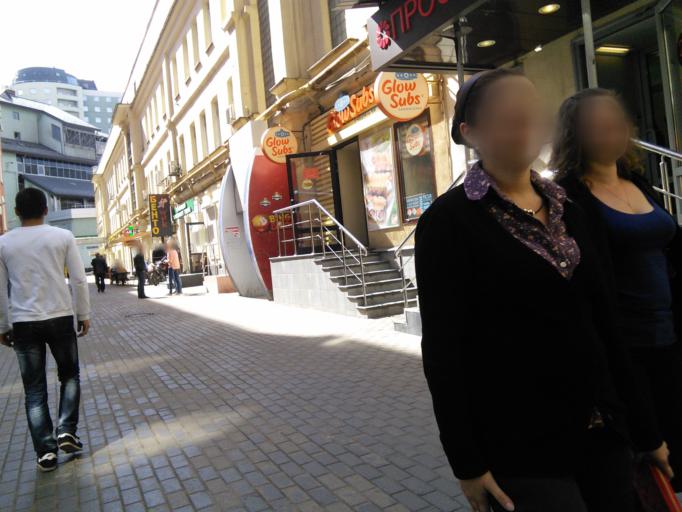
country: RU
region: Moscow
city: Mar'ina Roshcha
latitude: 55.7819
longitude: 37.6014
